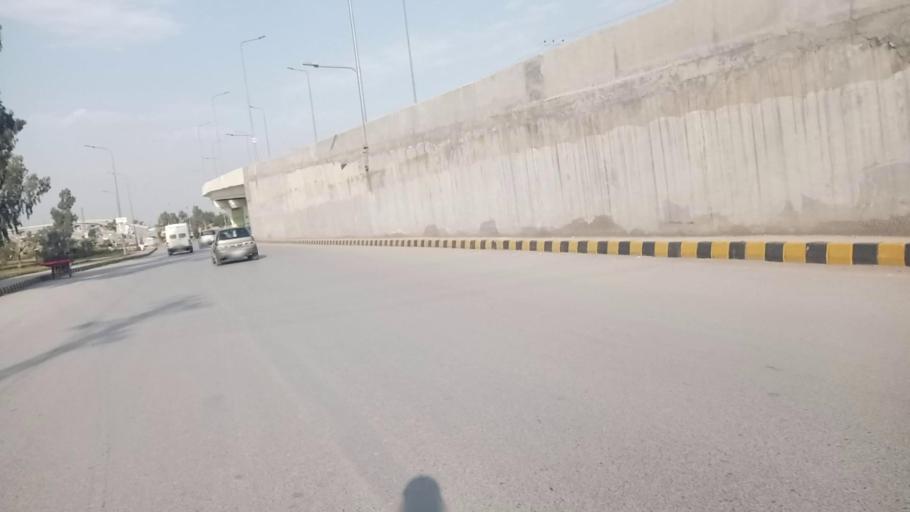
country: PK
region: Khyber Pakhtunkhwa
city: Peshawar
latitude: 33.9912
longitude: 71.4557
